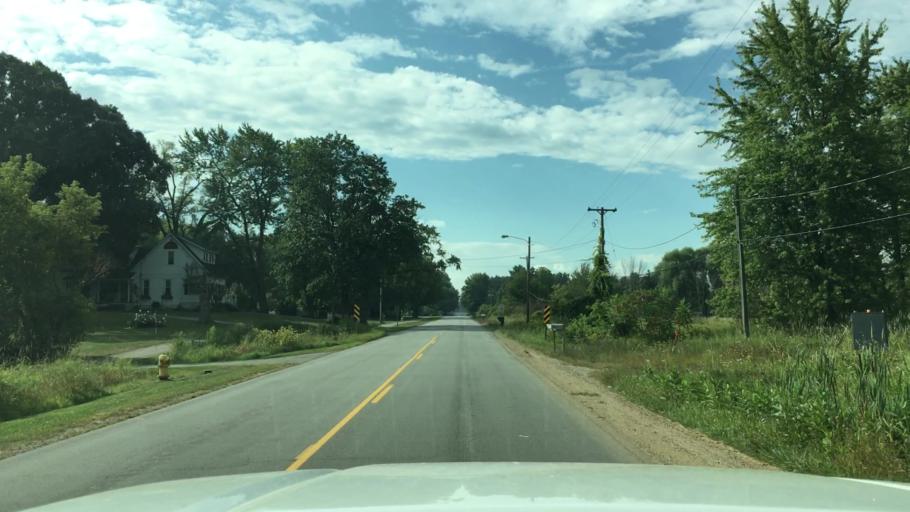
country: US
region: Michigan
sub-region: Ottawa County
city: Hudsonville
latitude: 42.8226
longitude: -85.8423
